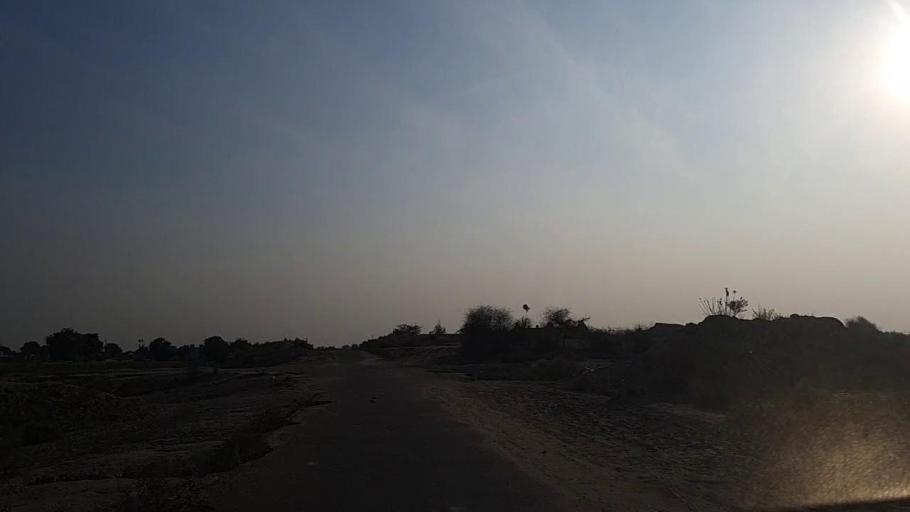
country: PK
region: Sindh
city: Jam Sahib
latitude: 26.4379
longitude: 68.5935
